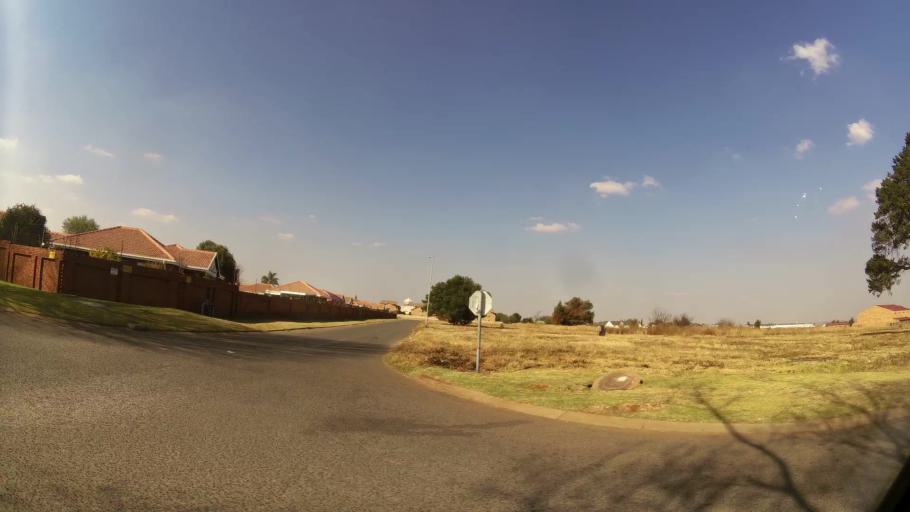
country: ZA
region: Gauteng
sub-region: Ekurhuleni Metropolitan Municipality
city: Brakpan
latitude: -26.2441
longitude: 28.3163
